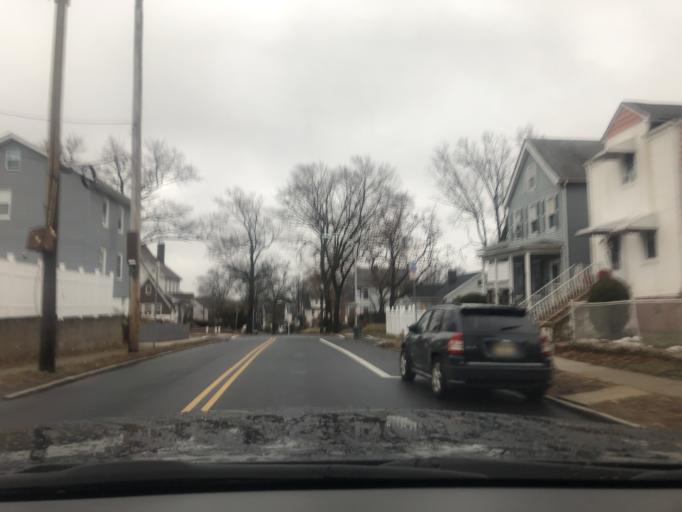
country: US
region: New Jersey
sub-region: Essex County
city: Orange
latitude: 40.7539
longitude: -74.2342
